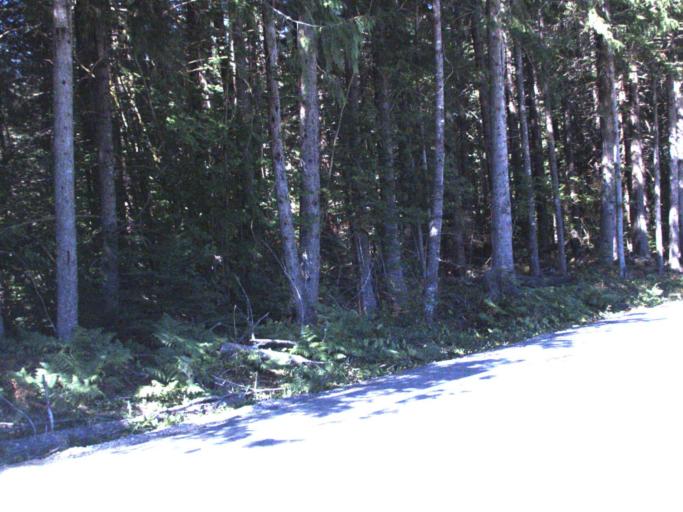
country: US
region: Washington
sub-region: King County
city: Riverbend
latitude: 47.1391
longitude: -121.6280
